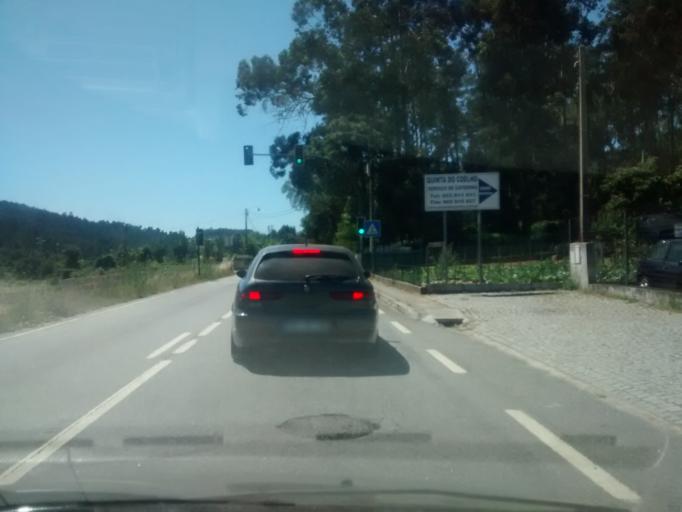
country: PT
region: Braga
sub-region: Barcelos
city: Galegos
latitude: 41.5300
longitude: -8.5377
